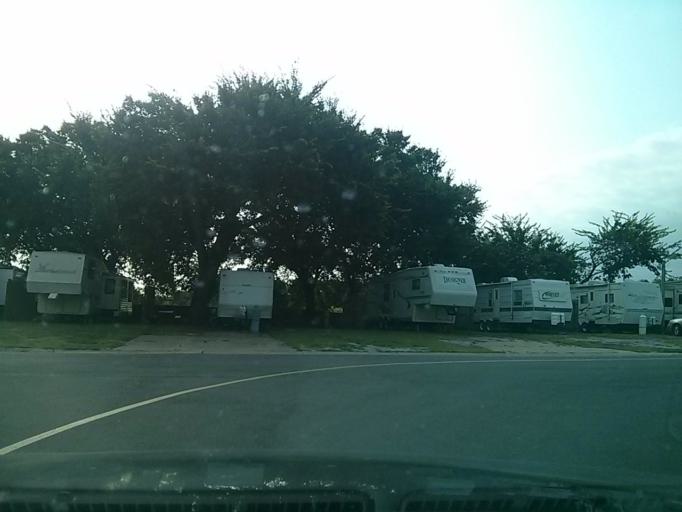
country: US
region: Oklahoma
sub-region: Tulsa County
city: Owasso
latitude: 36.1676
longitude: -95.8663
